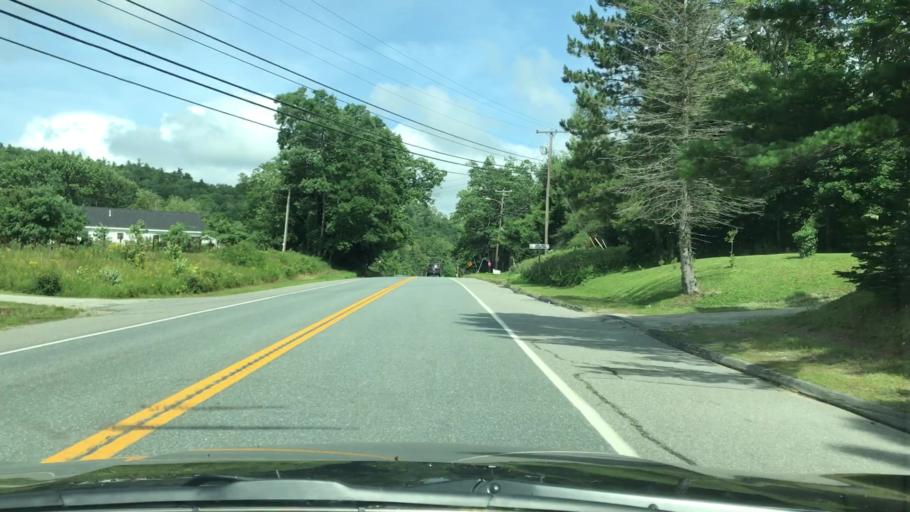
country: US
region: Maine
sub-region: Hancock County
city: Orland
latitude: 44.5671
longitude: -68.6809
